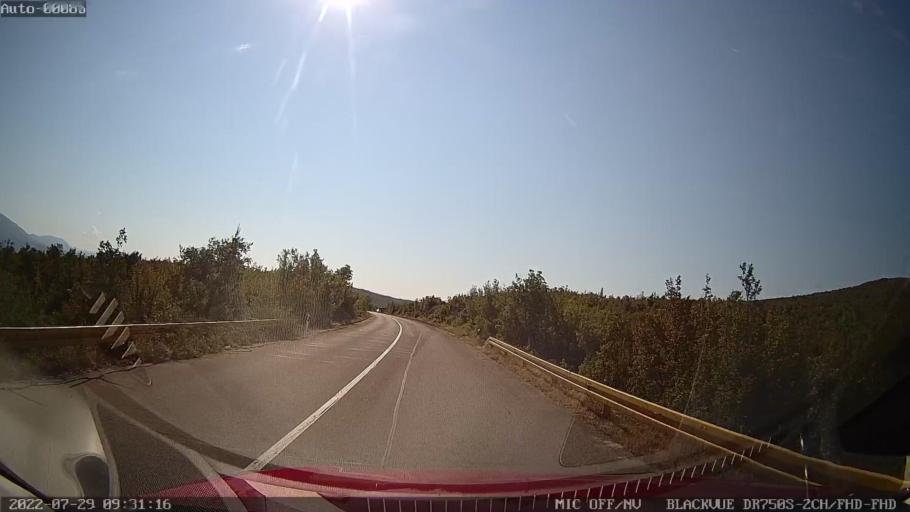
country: HR
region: Zadarska
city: Obrovac
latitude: 44.1900
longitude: 15.6967
